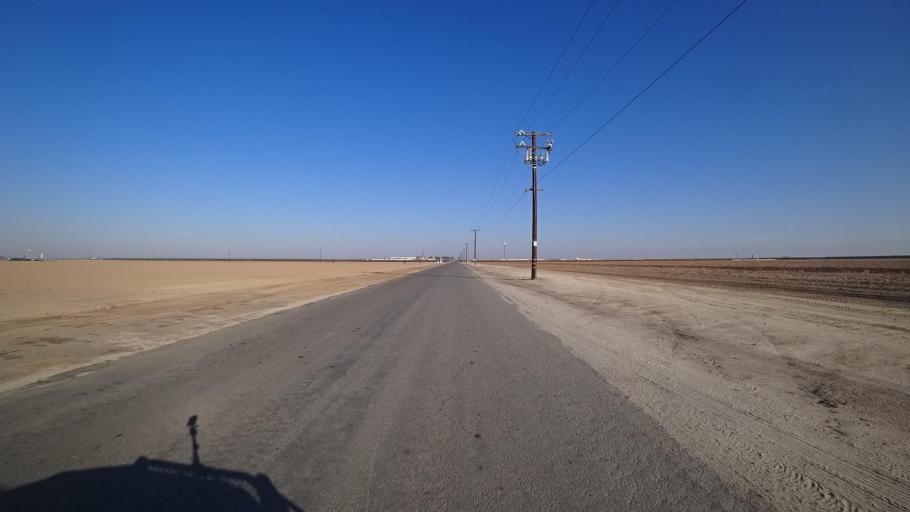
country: US
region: California
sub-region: Tulare County
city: Richgrove
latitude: 35.7772
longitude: -119.1607
